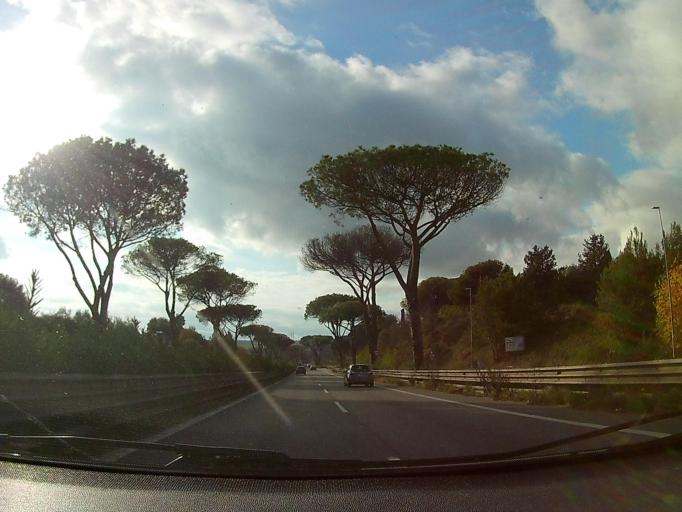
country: IT
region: Latium
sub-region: Citta metropolitana di Roma Capitale
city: Vitinia
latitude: 41.7909
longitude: 12.4284
